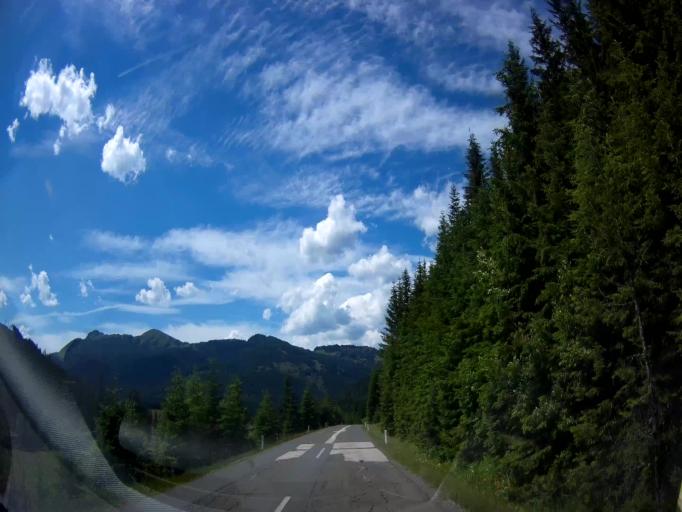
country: AT
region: Styria
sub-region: Politischer Bezirk Murau
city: Stadl an der Mur
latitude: 46.9652
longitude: 14.0209
